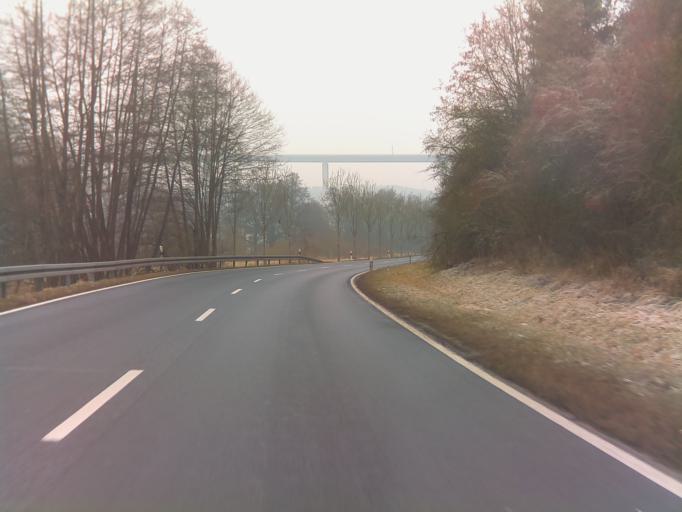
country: DE
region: Thuringia
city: Schwarza
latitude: 50.6050
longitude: 10.5212
